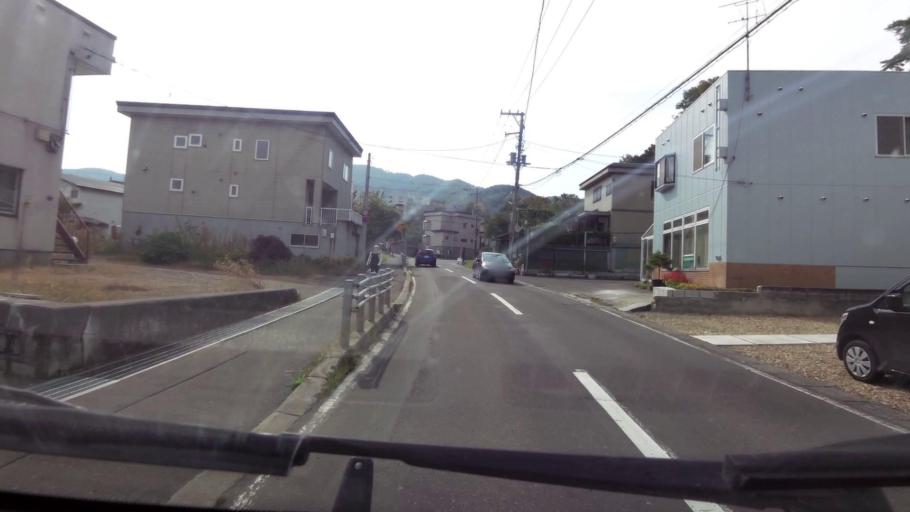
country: JP
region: Hokkaido
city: Otaru
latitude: 43.1433
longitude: 141.1576
